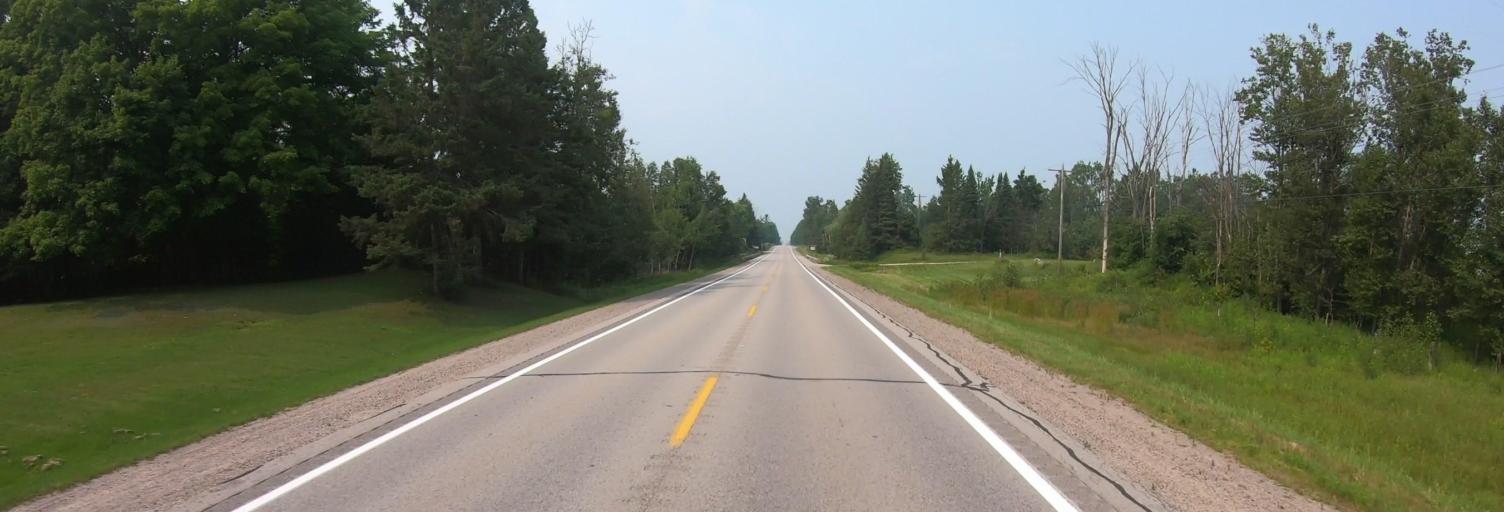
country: US
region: Michigan
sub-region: Chippewa County
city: Sault Ste. Marie
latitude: 46.2411
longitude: -84.3634
